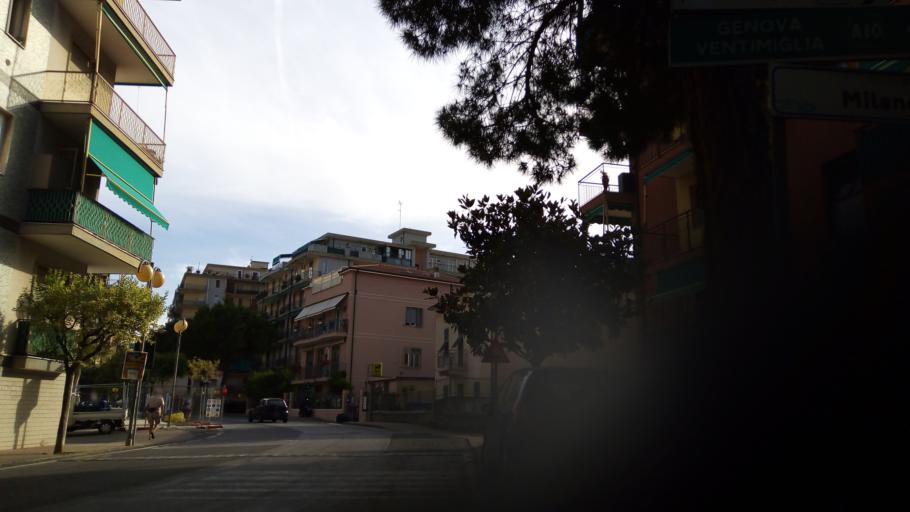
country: IT
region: Liguria
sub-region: Provincia di Savona
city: Borghetto Santo Spirito
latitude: 44.1152
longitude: 8.2450
